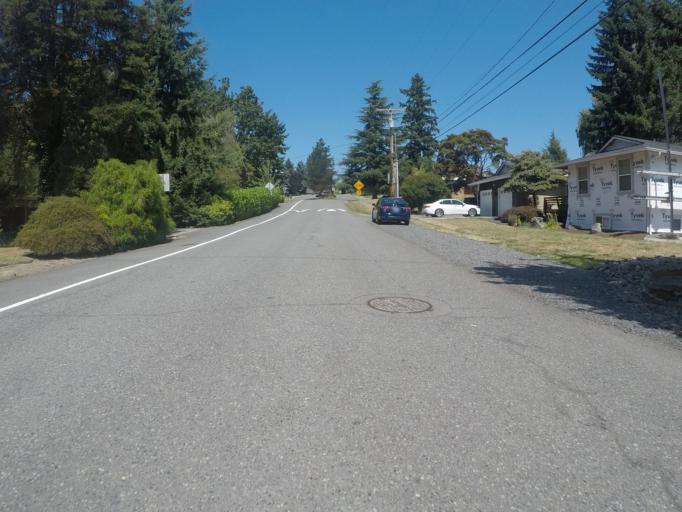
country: US
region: Washington
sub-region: King County
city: Kenmore
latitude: 47.7654
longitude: -122.2571
